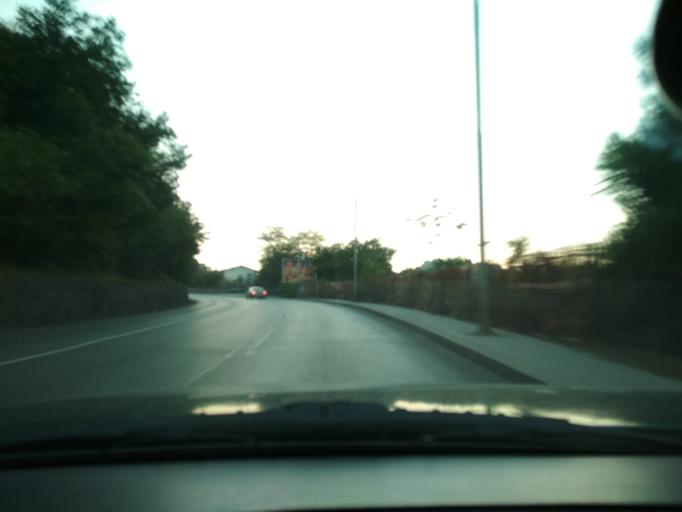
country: ME
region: Herceg Novi
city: Herceg-Novi
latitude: 42.4550
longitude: 18.5486
